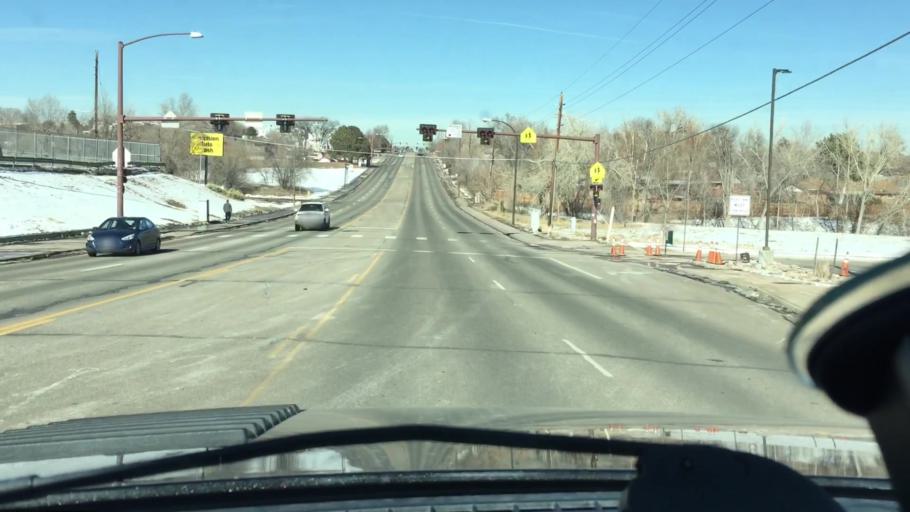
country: US
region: Colorado
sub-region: Adams County
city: Federal Heights
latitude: 39.8501
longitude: -104.9966
